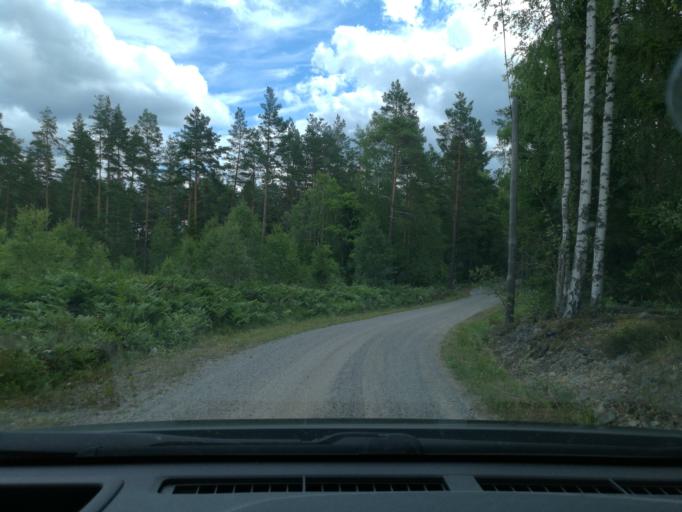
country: SE
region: Stockholm
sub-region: Sigtuna Kommun
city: Marsta
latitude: 59.6668
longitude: 17.8900
